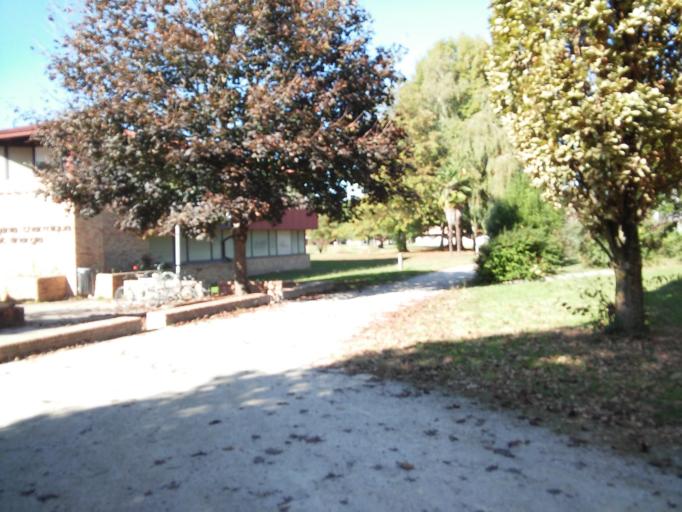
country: FR
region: Aquitaine
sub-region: Departement des Pyrenees-Atlantiques
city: Pau
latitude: 43.3134
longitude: -0.3656
